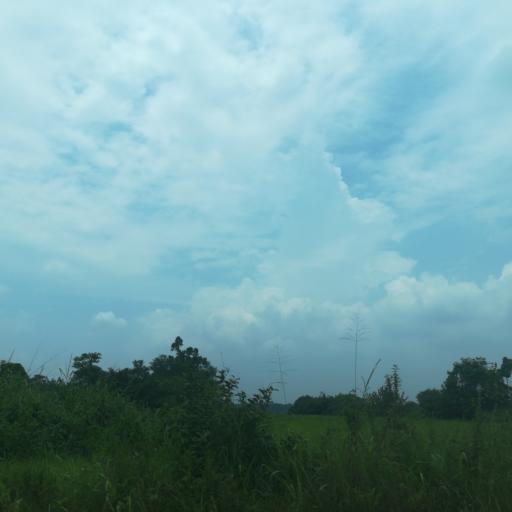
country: NG
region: Lagos
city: Ejirin
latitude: 6.6761
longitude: 3.8005
